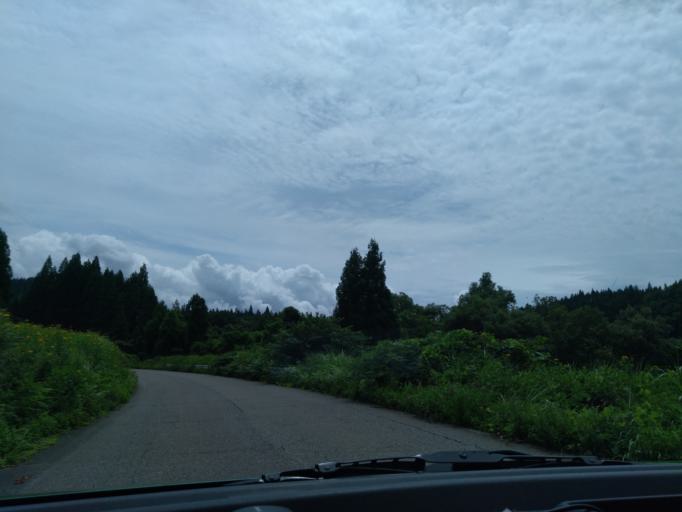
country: JP
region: Akita
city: Kakunodatemachi
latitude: 39.5716
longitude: 140.6335
